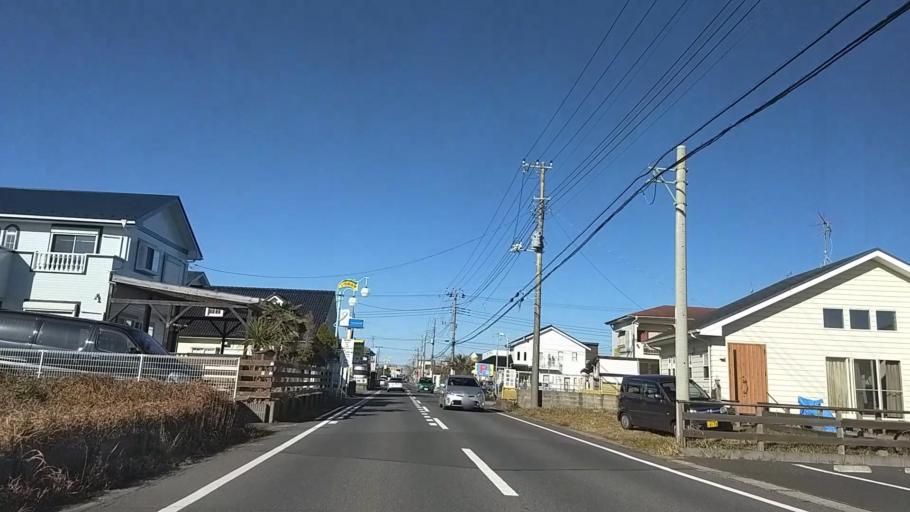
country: JP
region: Chiba
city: Ohara
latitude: 35.3557
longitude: 140.3888
